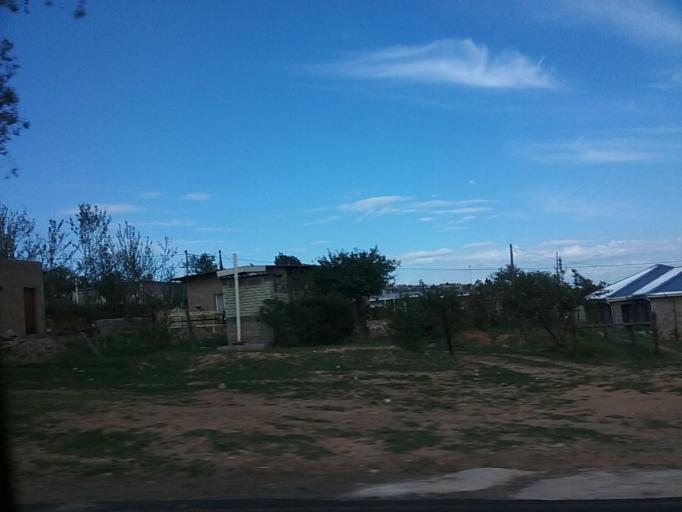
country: LS
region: Berea
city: Teyateyaneng
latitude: -29.1348
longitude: 27.7586
